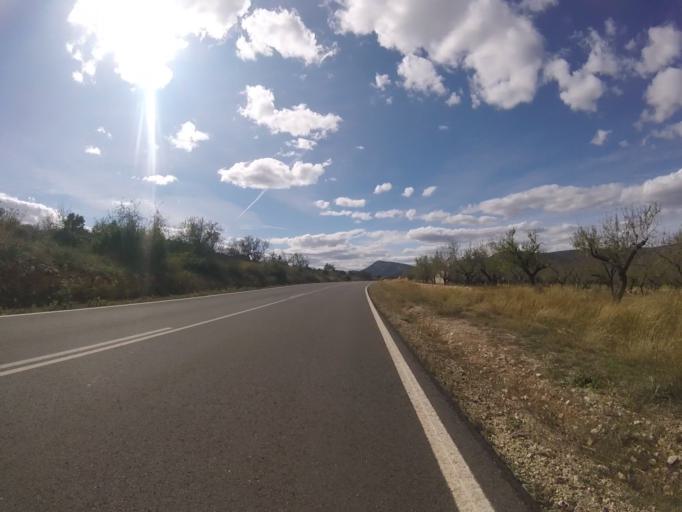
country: ES
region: Valencia
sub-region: Provincia de Castello
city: Cati
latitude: 40.4251
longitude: 0.0850
